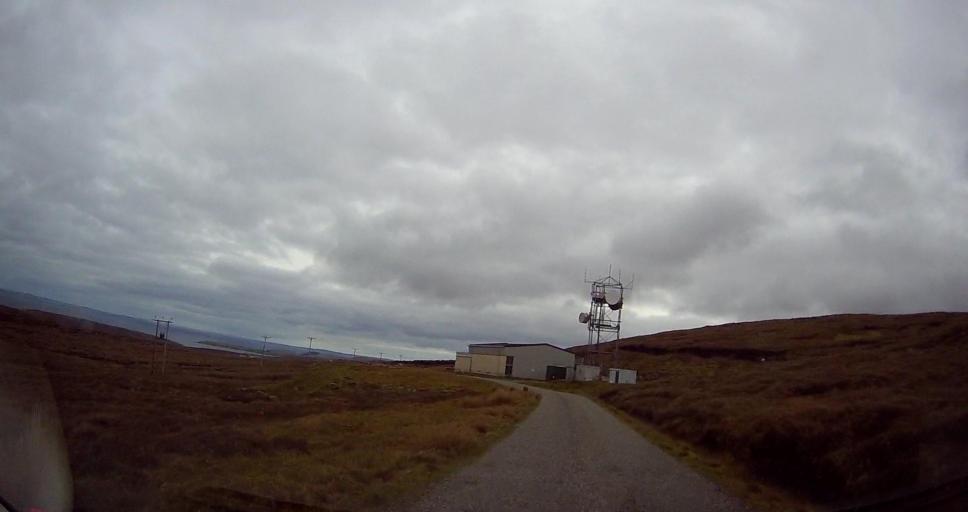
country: GB
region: Scotland
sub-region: Shetland Islands
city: Shetland
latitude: 60.5750
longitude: -1.0676
